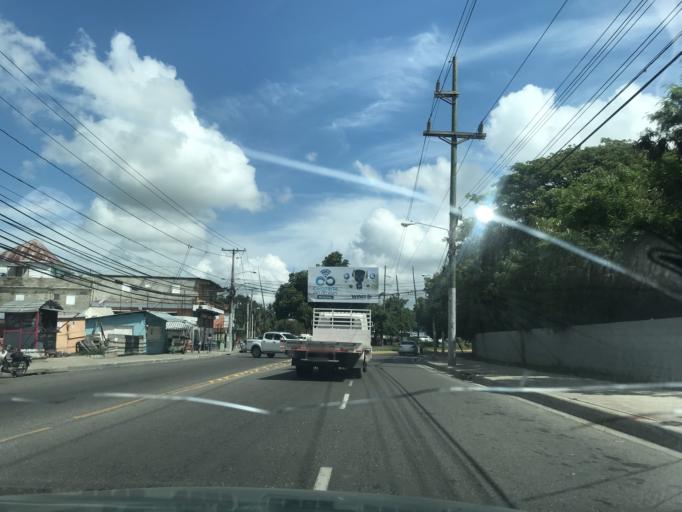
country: DO
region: Santiago
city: Palmar Arriba
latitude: 19.4919
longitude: -70.7368
